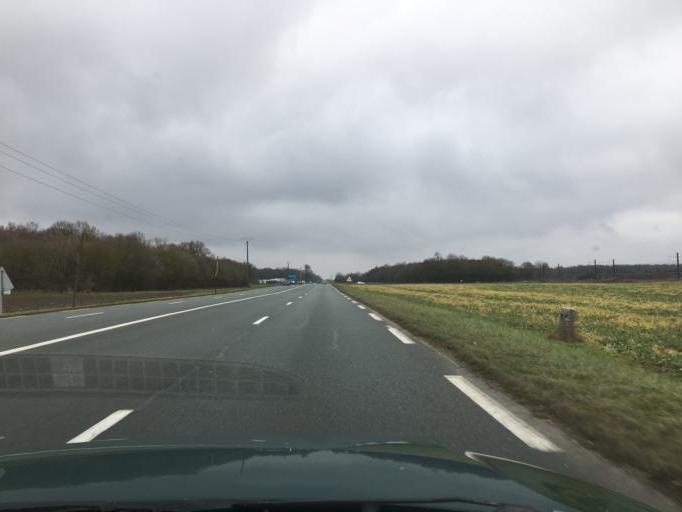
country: FR
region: Centre
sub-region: Departement du Loiret
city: Chevilly
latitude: 47.9962
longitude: 1.8811
